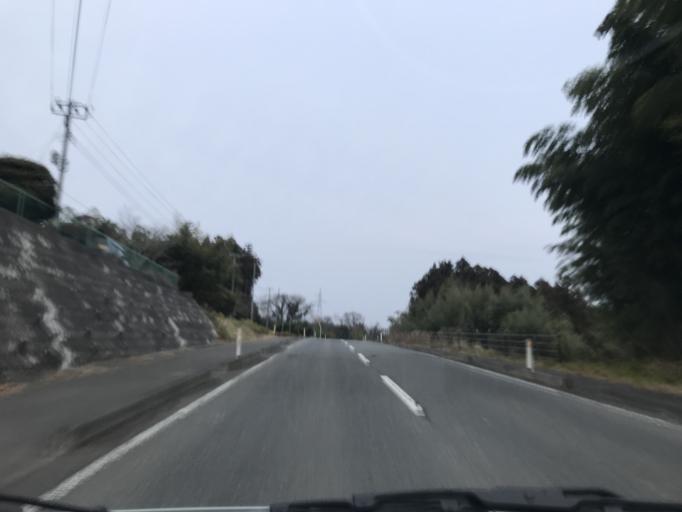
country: JP
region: Miyagi
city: Wakuya
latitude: 38.7138
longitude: 141.1297
